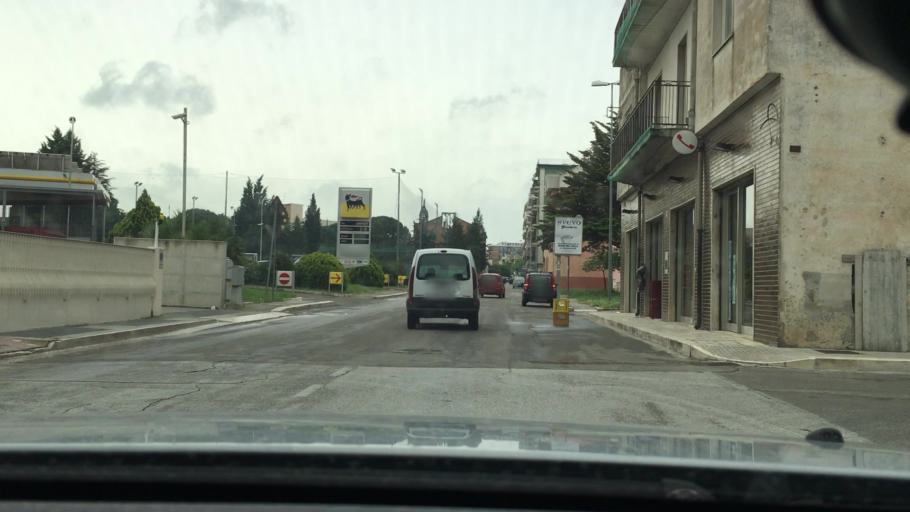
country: IT
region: Apulia
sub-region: Provincia di Bari
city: Gioia del Colle
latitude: 40.8063
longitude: 16.9241
